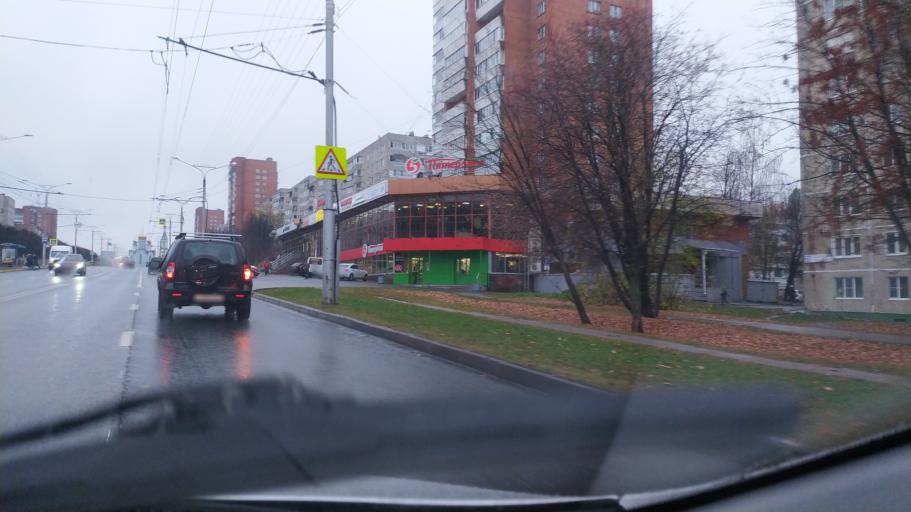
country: RU
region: Chuvashia
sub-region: Cheboksarskiy Rayon
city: Cheboksary
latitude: 56.1465
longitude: 47.1860
